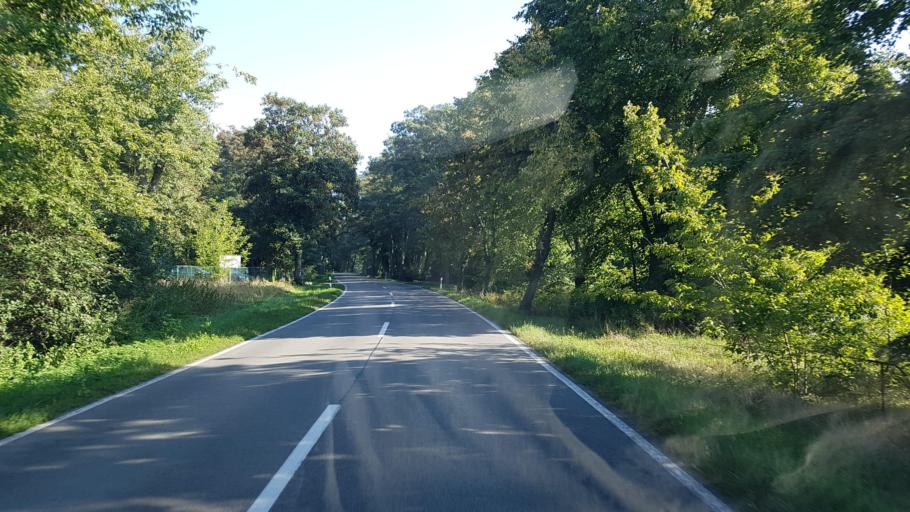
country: DE
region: Brandenburg
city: Brandenburg an der Havel
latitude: 52.4856
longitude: 12.5976
